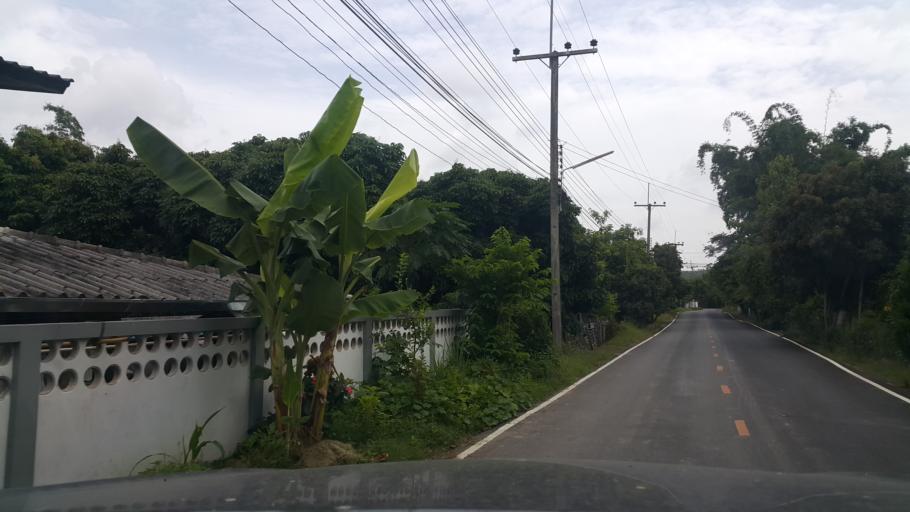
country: TH
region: Lamphun
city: Ban Thi
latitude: 18.6645
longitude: 99.1531
